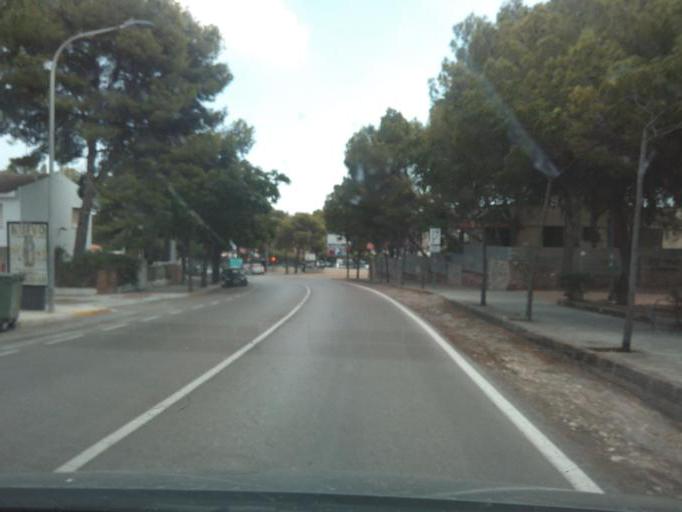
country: ES
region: Valencia
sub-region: Provincia de Valencia
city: Manises
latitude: 39.5288
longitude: -0.4856
